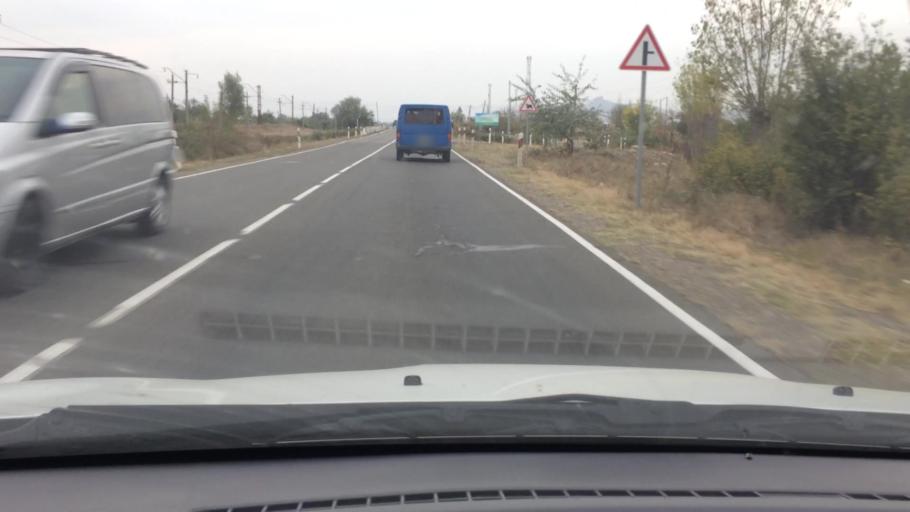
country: GE
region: Kvemo Kartli
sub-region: Marneuli
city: Marneuli
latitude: 41.4414
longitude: 44.8171
